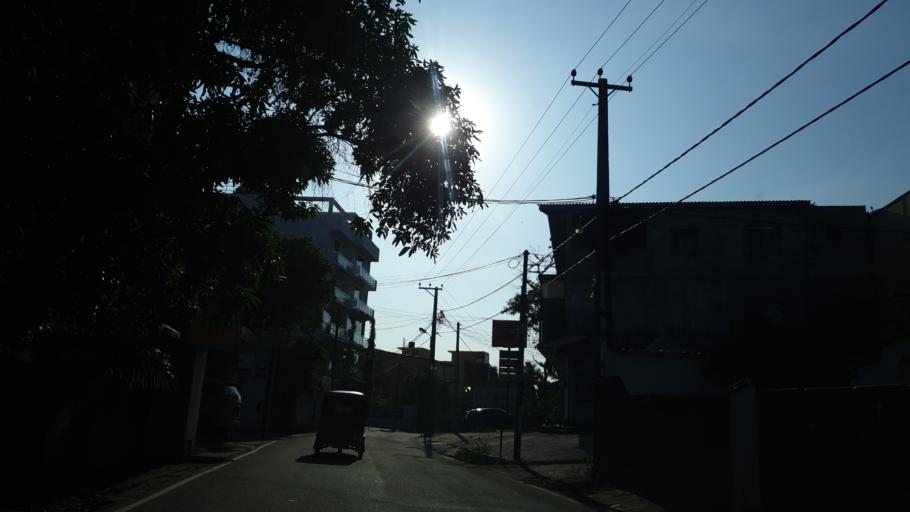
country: LK
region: Western
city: Galkissa
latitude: 6.8525
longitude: 79.8836
